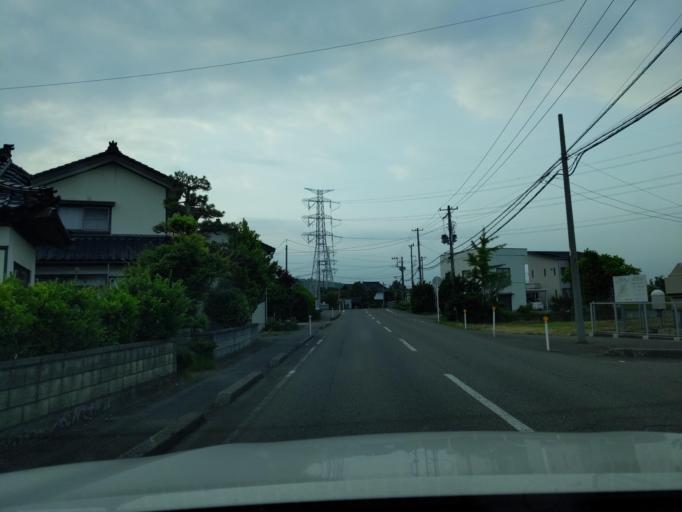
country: JP
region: Niigata
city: Kashiwazaki
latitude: 37.4088
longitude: 138.6071
